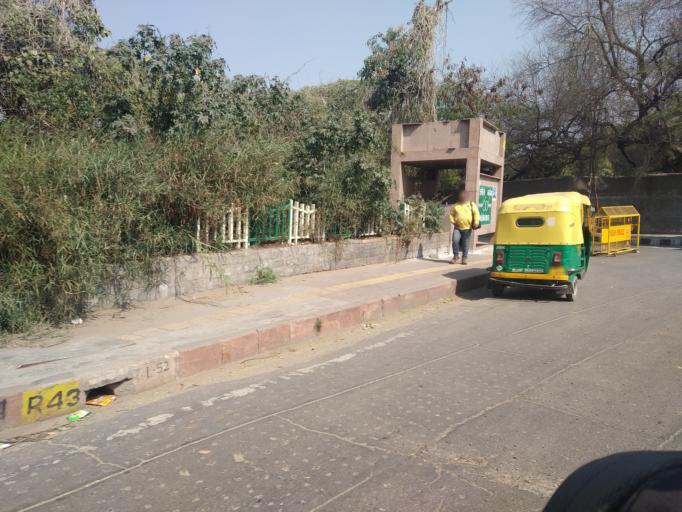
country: IN
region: NCT
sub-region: North Delhi
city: Delhi
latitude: 28.6683
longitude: 77.2237
